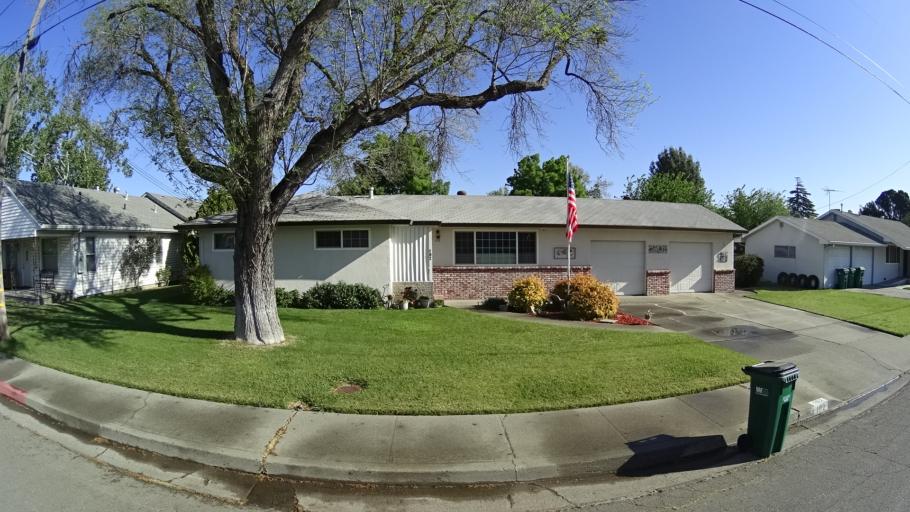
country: US
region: California
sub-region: Glenn County
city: Orland
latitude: 39.7416
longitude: -122.1905
